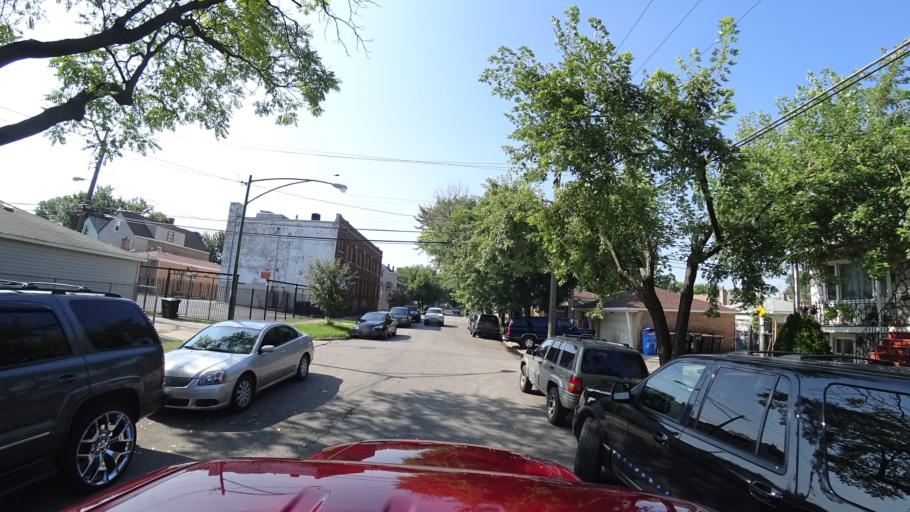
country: US
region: Illinois
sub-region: Cook County
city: Cicero
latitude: 41.8249
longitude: -87.7094
